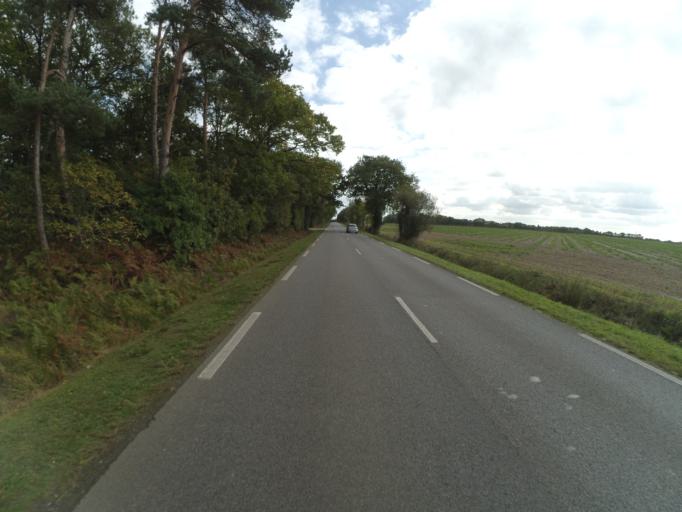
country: FR
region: Pays de la Loire
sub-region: Departement de la Loire-Atlantique
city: Plesse
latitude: 47.4929
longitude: -1.8606
